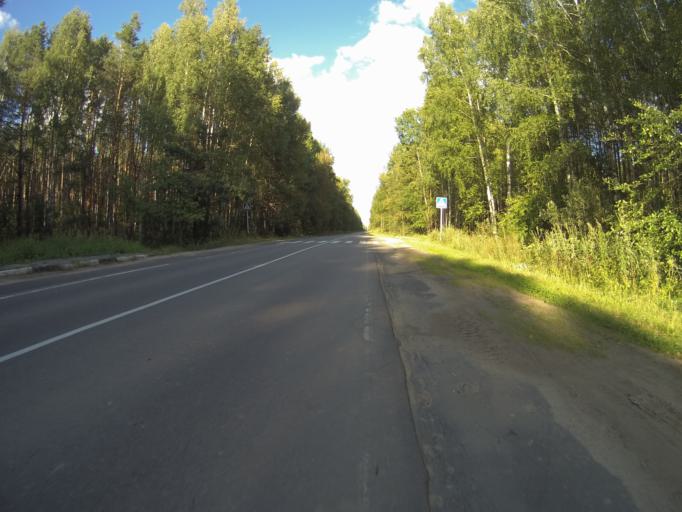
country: RU
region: Vladimir
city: Gusevskiy
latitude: 55.5784
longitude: 40.5291
